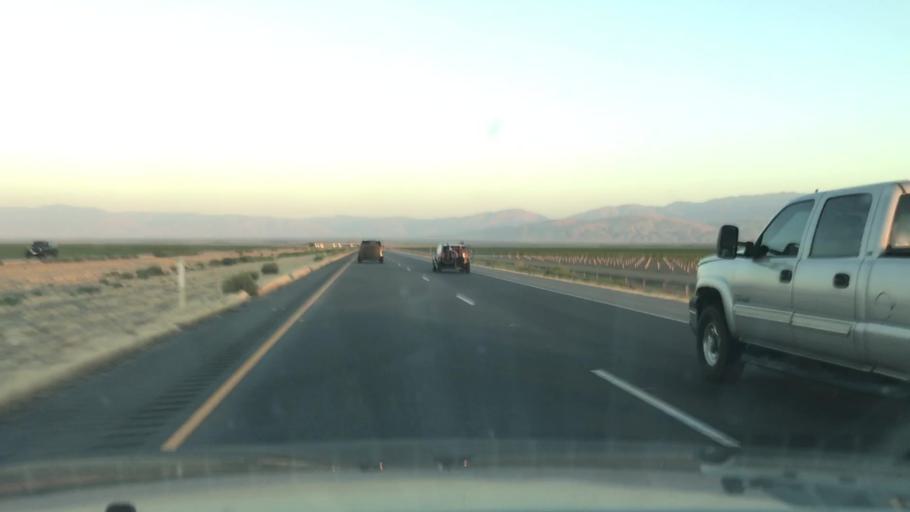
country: US
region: California
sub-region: Kern County
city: Greenfield
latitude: 35.1395
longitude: -119.0866
